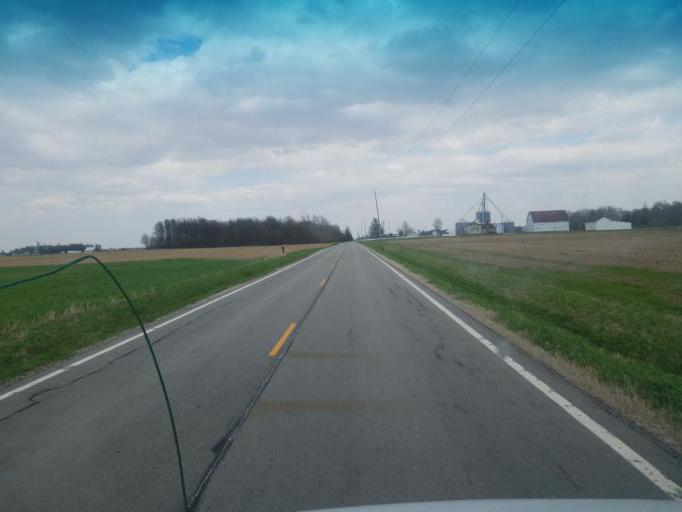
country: US
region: Ohio
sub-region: Crawford County
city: Bucyrus
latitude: 40.9504
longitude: -83.0315
